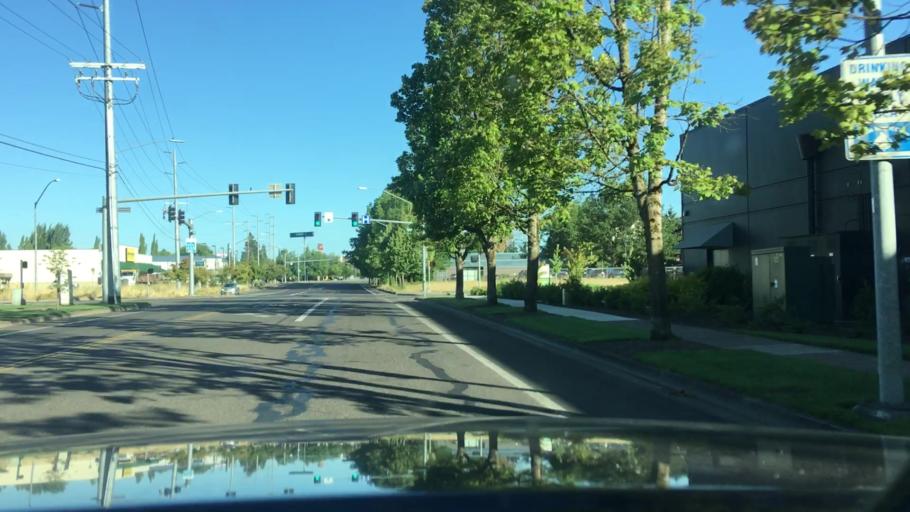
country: US
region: Oregon
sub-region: Lane County
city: Springfield
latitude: 44.0876
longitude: -123.0447
